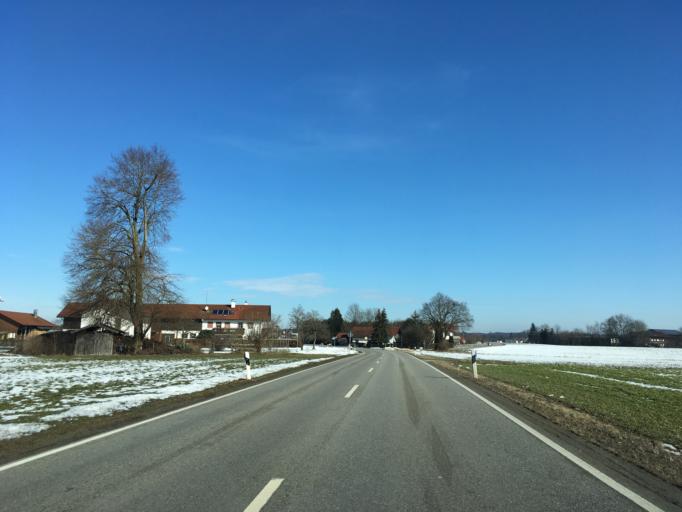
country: DE
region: Bavaria
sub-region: Upper Bavaria
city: Breitbrunn
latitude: 48.0485
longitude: 12.1570
